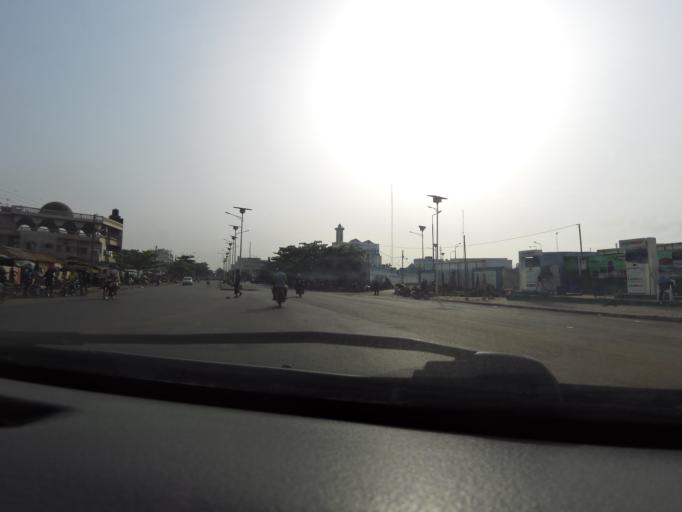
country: BJ
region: Littoral
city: Cotonou
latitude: 6.3565
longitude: 2.4249
